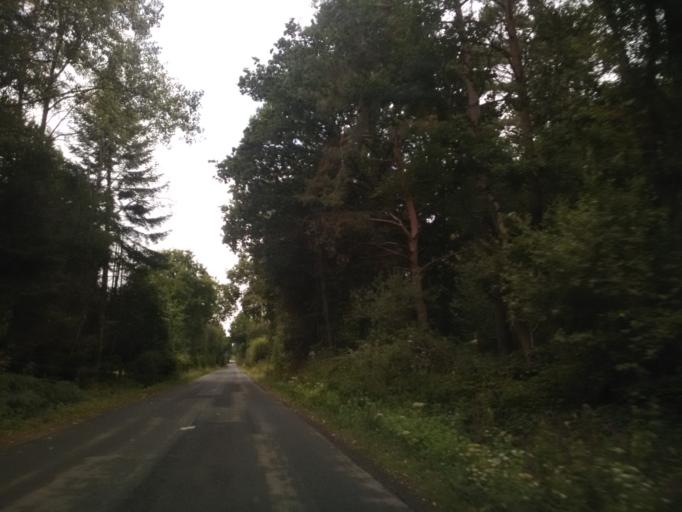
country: FR
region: Brittany
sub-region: Departement d'Ille-et-Vilaine
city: Dinge
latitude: 48.3520
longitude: -1.7702
